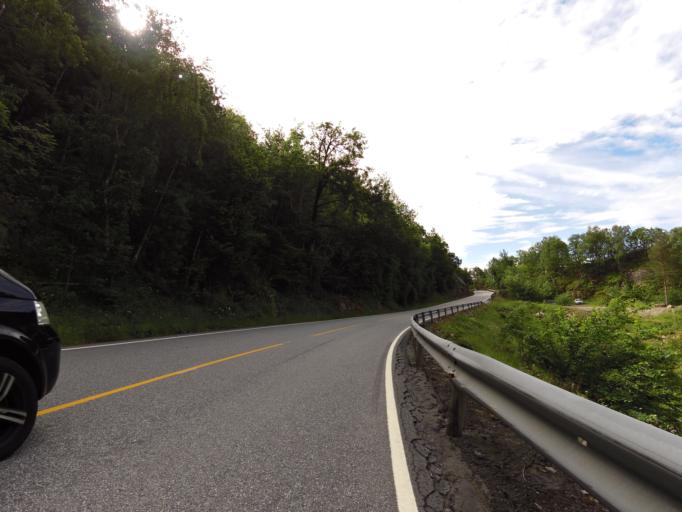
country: NO
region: Vest-Agder
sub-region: Lindesnes
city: Vigeland
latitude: 58.0556
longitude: 7.1817
